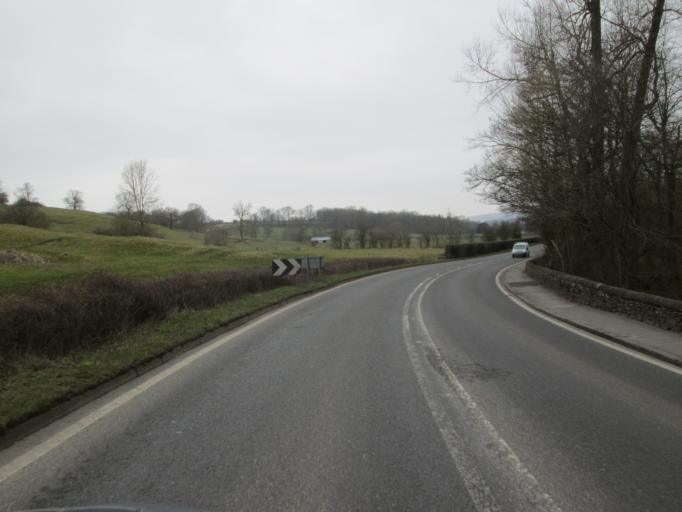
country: GB
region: England
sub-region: Derbyshire
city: Bakewell
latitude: 53.1954
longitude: -1.6583
